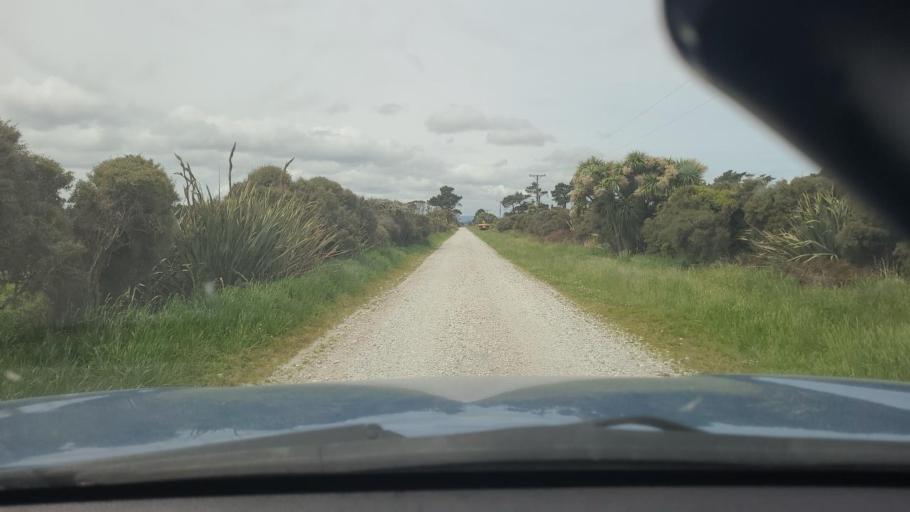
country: NZ
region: Southland
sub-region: Invercargill City
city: Bluff
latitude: -46.5606
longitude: 168.6899
